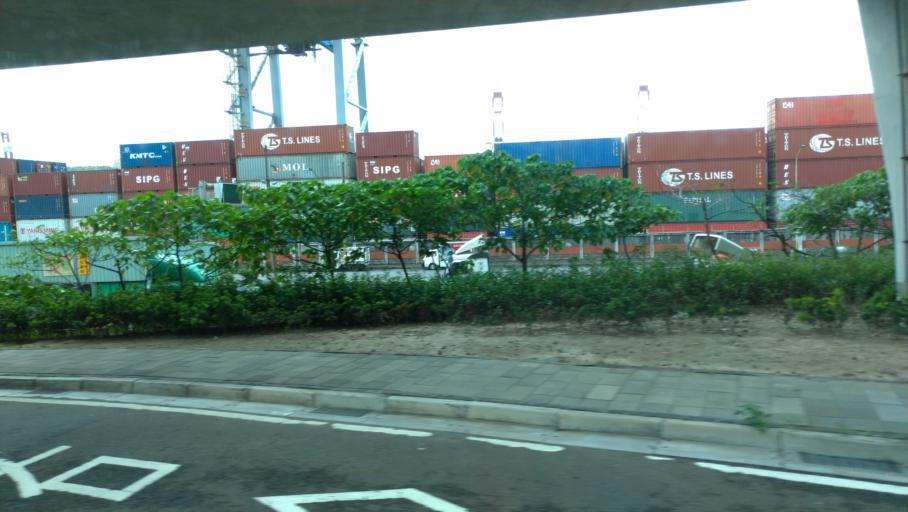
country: TW
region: Taiwan
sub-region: Keelung
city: Keelung
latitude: 25.1405
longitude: 121.7553
